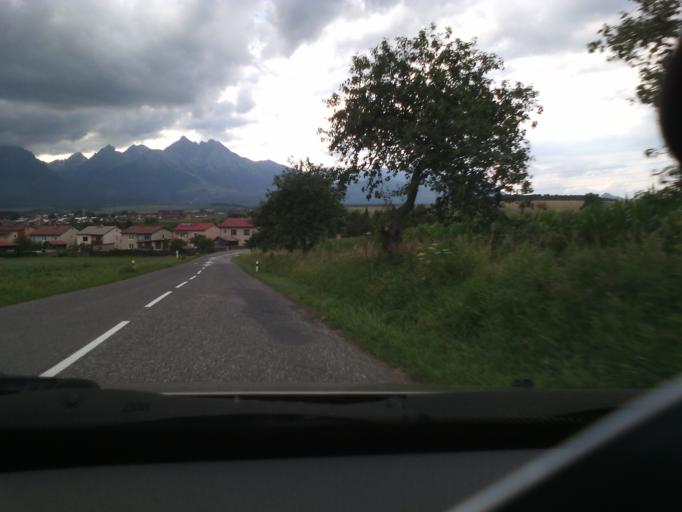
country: SK
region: Presovsky
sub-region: Okres Presov
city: Kezmarok
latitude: 49.1090
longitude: 20.3794
